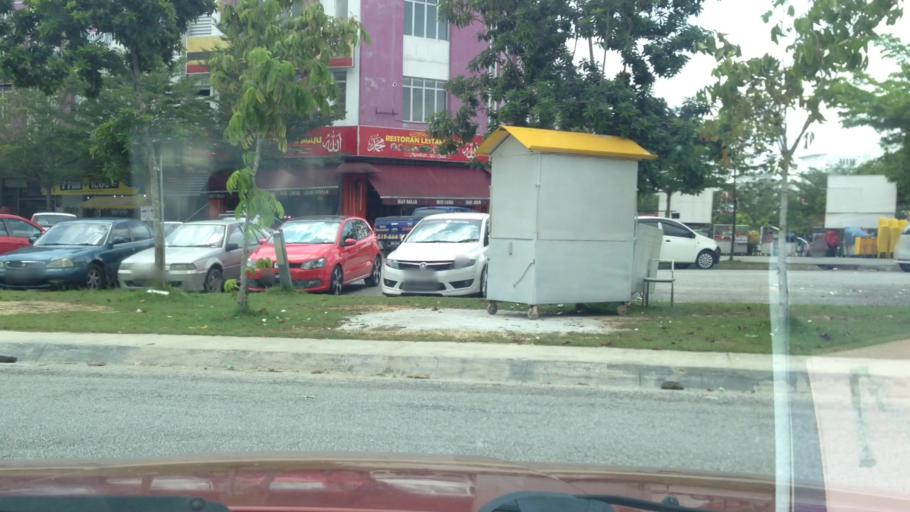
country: MY
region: Selangor
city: Kampung Baru Subang
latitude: 3.1774
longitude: 101.5485
